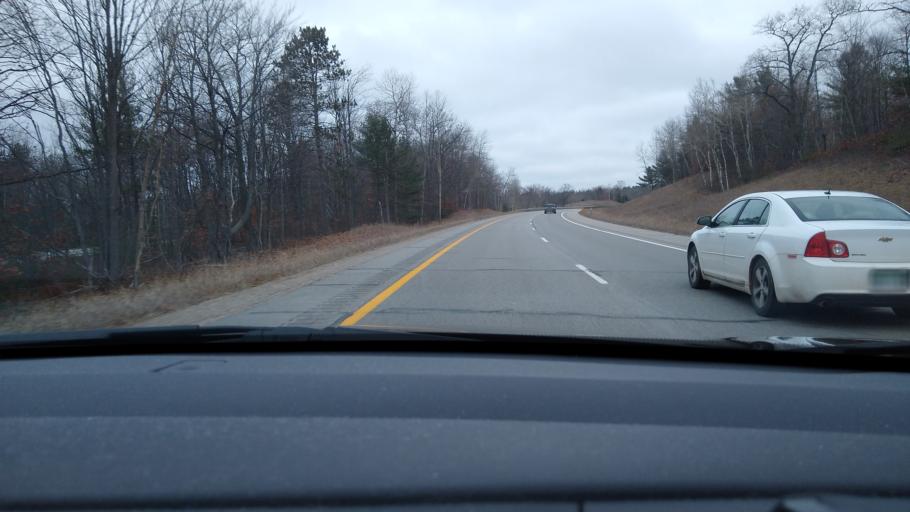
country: US
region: Michigan
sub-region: Otsego County
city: Gaylord
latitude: 44.9074
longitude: -84.6919
